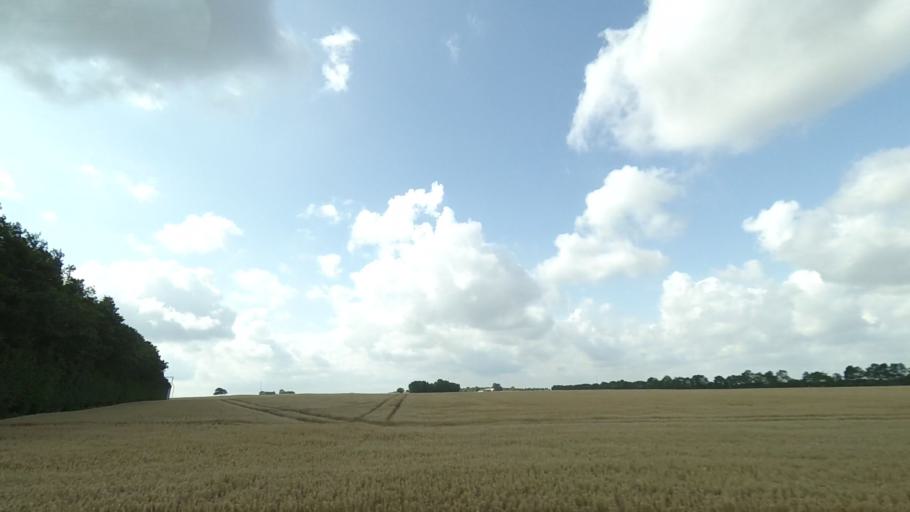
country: DK
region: Central Jutland
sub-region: Norddjurs Kommune
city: Auning
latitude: 56.4984
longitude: 10.4358
